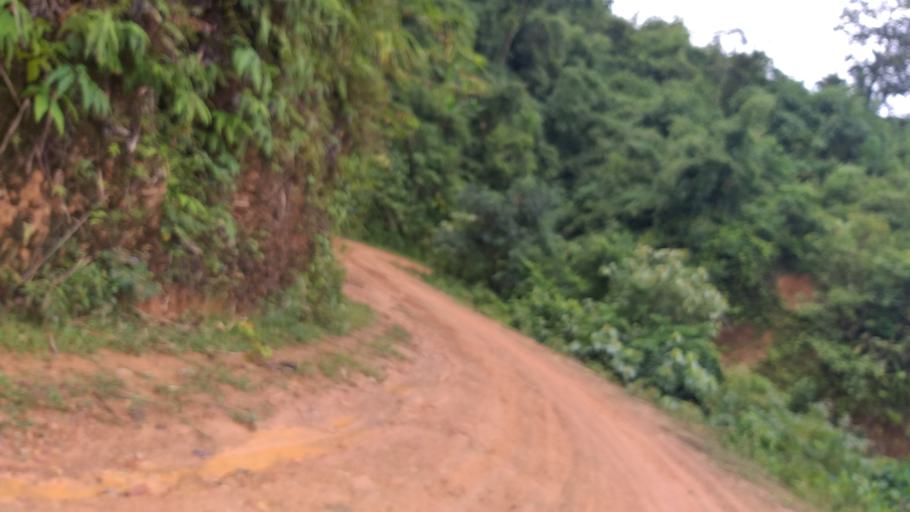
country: LA
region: Phongsali
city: Khoa
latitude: 21.3646
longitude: 102.6227
